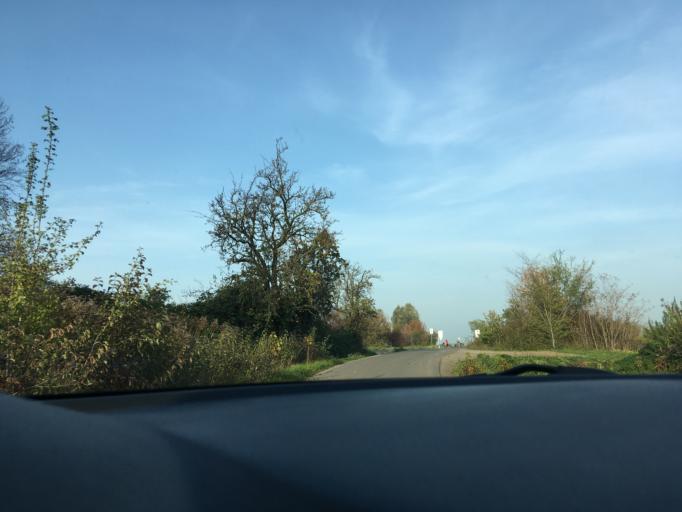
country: DE
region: Saxony
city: Espenhain
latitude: 51.1766
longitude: 12.4529
